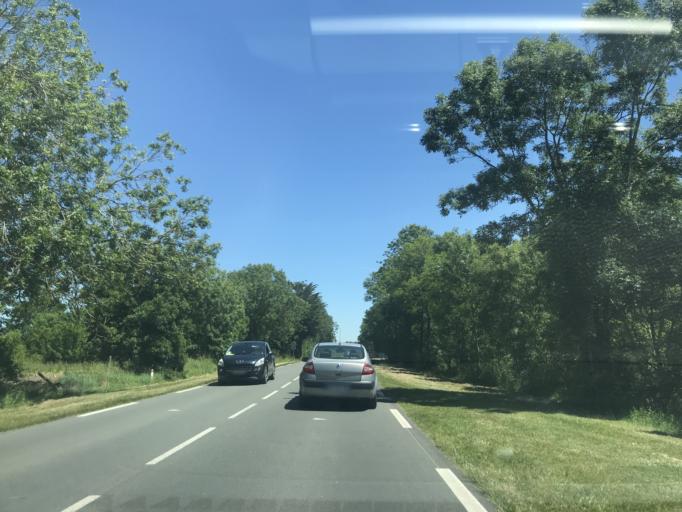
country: FR
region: Poitou-Charentes
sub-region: Departement de la Charente-Maritime
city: Meschers-sur-Gironde
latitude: 45.5636
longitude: -0.9484
